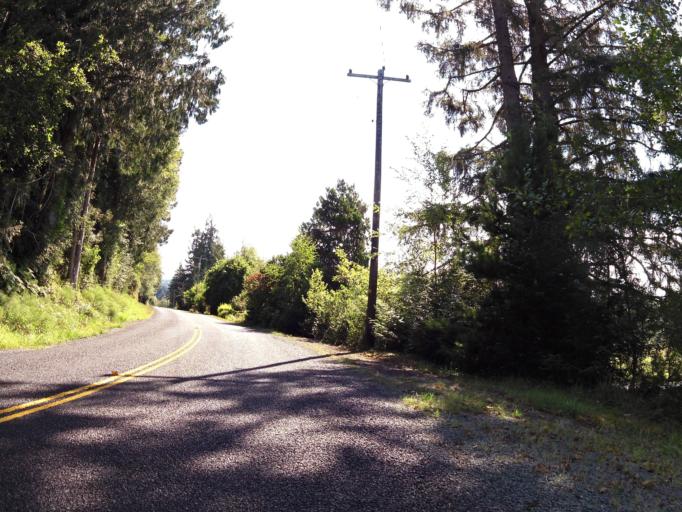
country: US
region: Washington
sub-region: Wahkiakum County
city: Cathlamet
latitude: 46.1863
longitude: -123.5818
